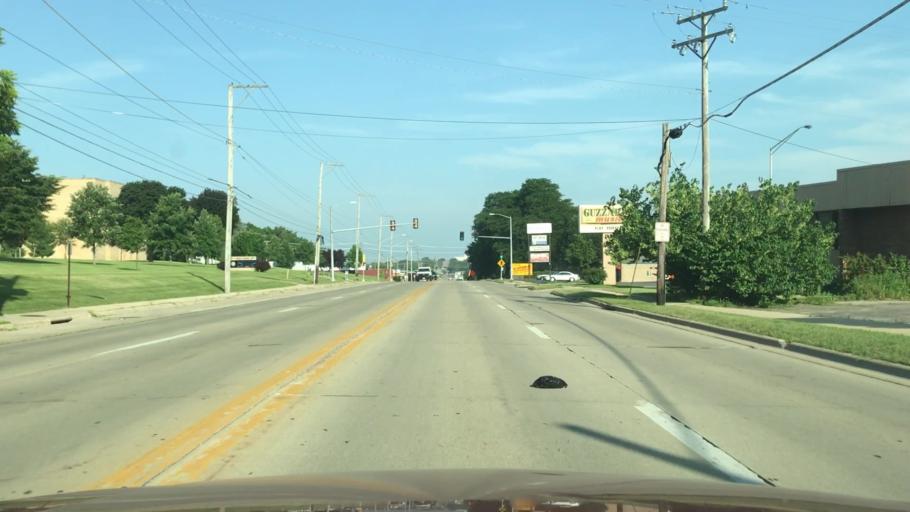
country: US
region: Illinois
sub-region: Winnebago County
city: Rockford
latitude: 42.2578
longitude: -89.0484
